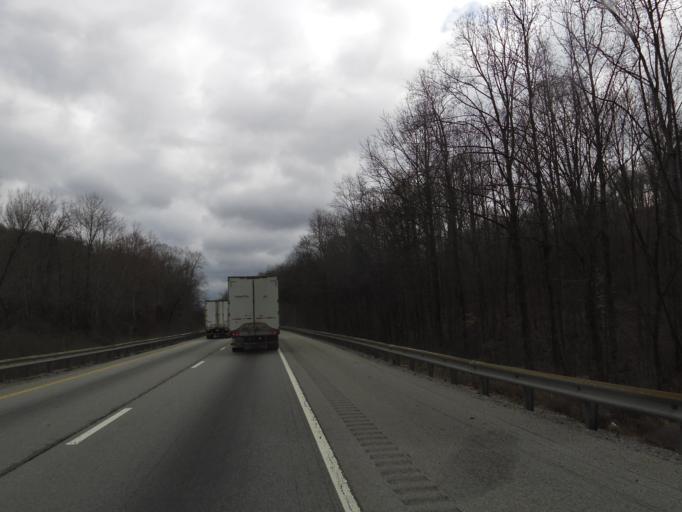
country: US
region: Tennessee
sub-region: Marion County
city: Jasper
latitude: 35.0349
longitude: -85.5953
